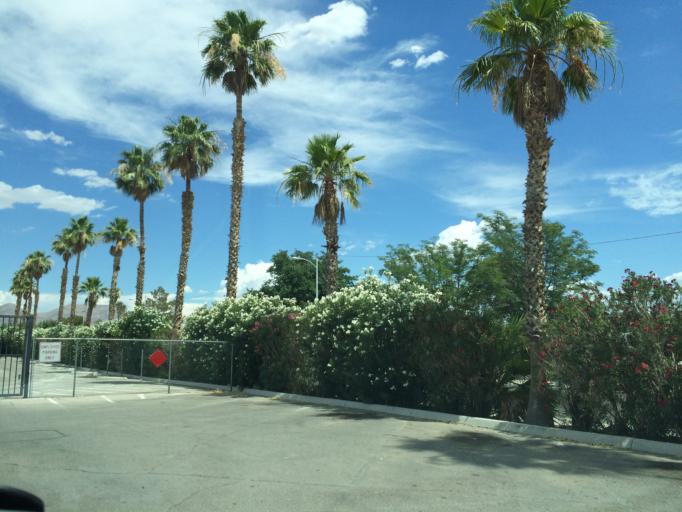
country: US
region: Nevada
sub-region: Clark County
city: North Las Vegas
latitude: 36.1945
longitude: -115.1250
